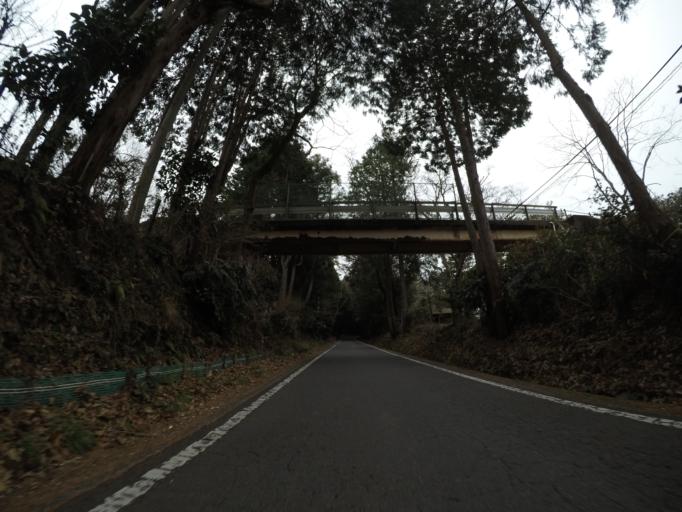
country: JP
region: Shizuoka
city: Fujinomiya
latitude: 35.2357
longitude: 138.5789
